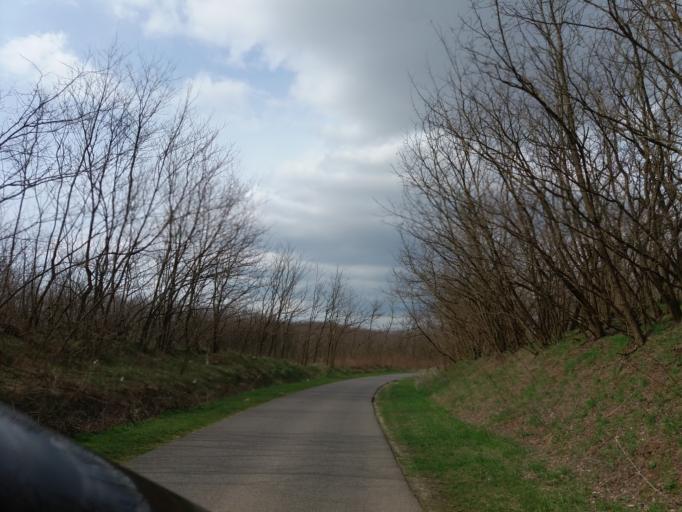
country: HU
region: Szabolcs-Szatmar-Bereg
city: Petnehaza
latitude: 48.0722
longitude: 22.0447
